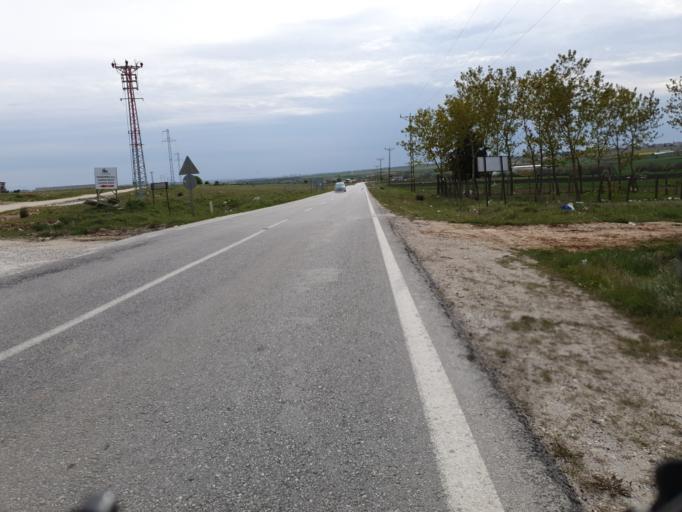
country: TR
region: Tekirdag
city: Velimese
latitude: 41.2941
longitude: 27.9323
